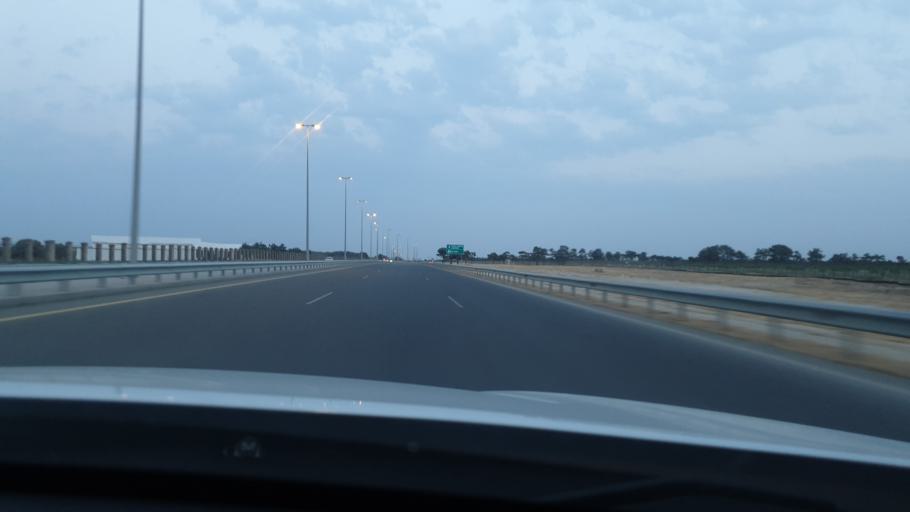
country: AZ
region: Baki
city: Bilajer
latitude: 40.5626
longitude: 50.0722
